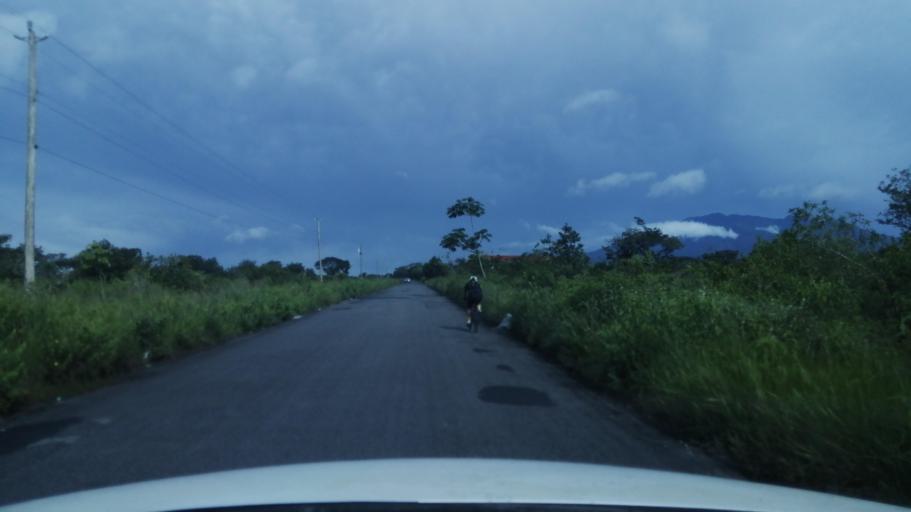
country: PA
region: Chiriqui
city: Potrerillos Abajo
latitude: 8.6693
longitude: -82.4320
